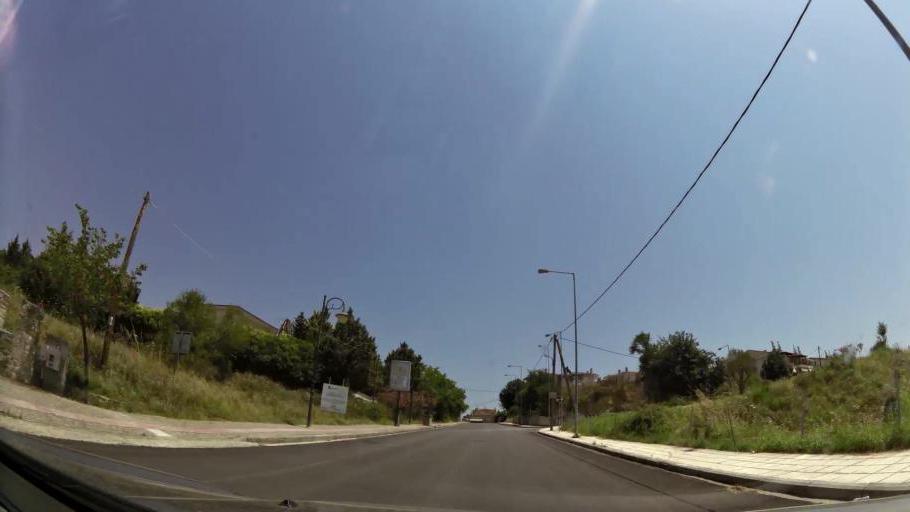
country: GR
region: Central Macedonia
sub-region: Nomos Thessalonikis
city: Trilofos
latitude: 40.4694
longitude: 22.9645
